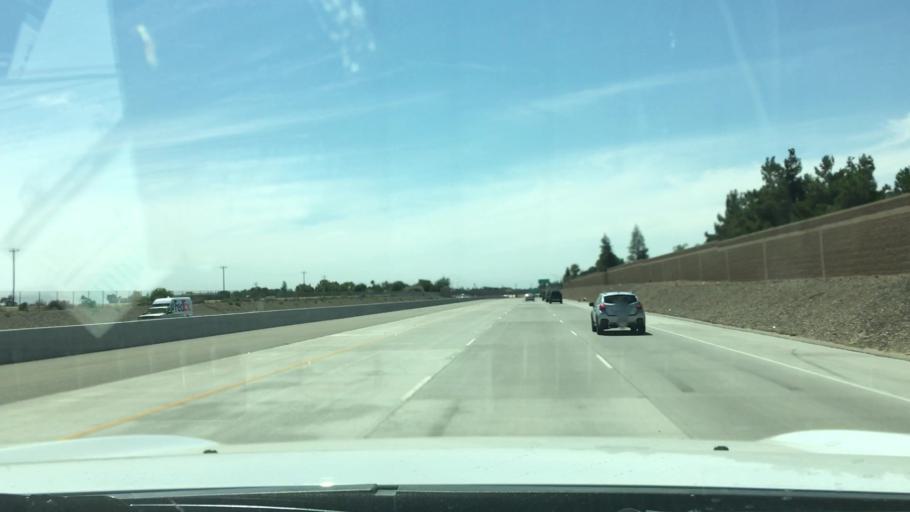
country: US
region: California
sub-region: Kern County
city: Greenacres
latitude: 35.3620
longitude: -119.1057
